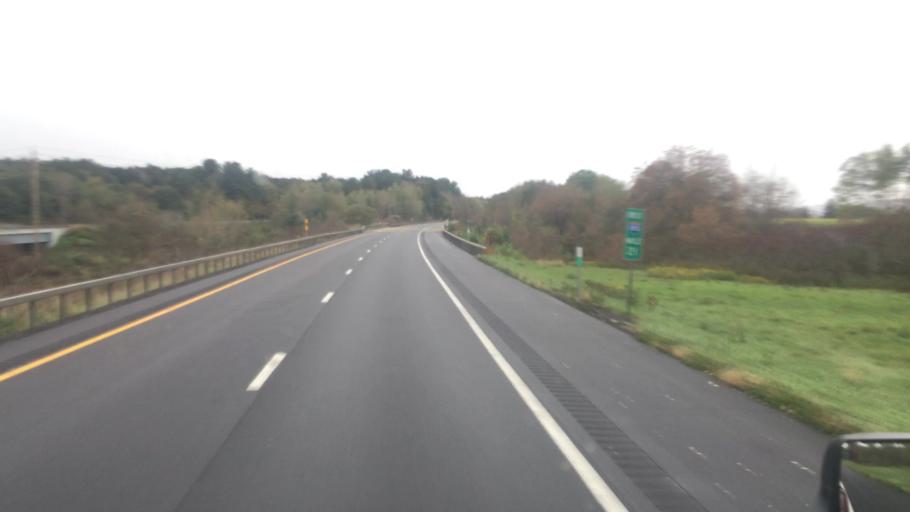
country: US
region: New York
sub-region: Chenango County
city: Bainbridge
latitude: 42.1982
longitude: -75.5417
